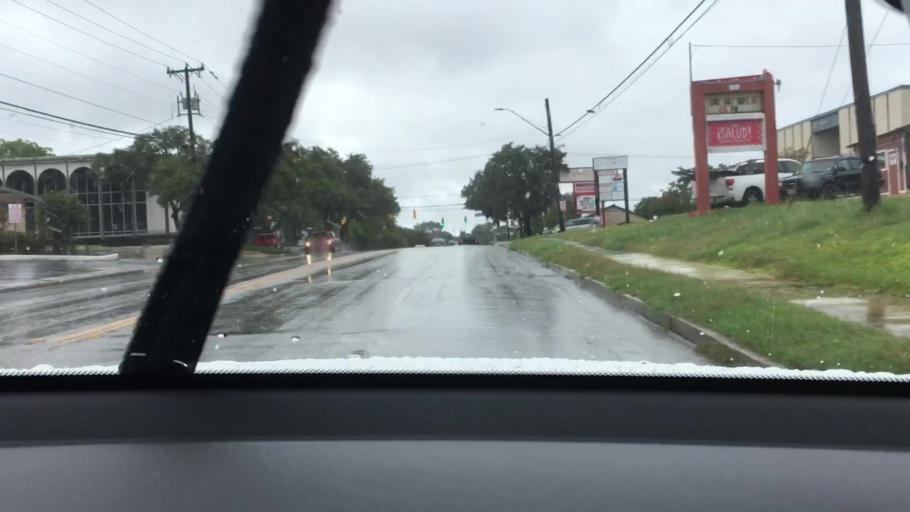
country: US
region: Texas
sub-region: Bexar County
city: Alamo Heights
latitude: 29.5108
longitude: -98.4662
